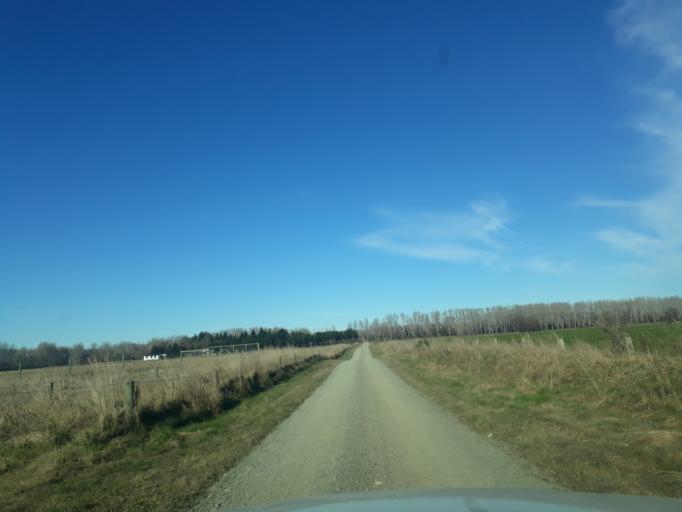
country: NZ
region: Canterbury
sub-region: Timaru District
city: Pleasant Point
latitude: -44.2544
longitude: 171.2190
